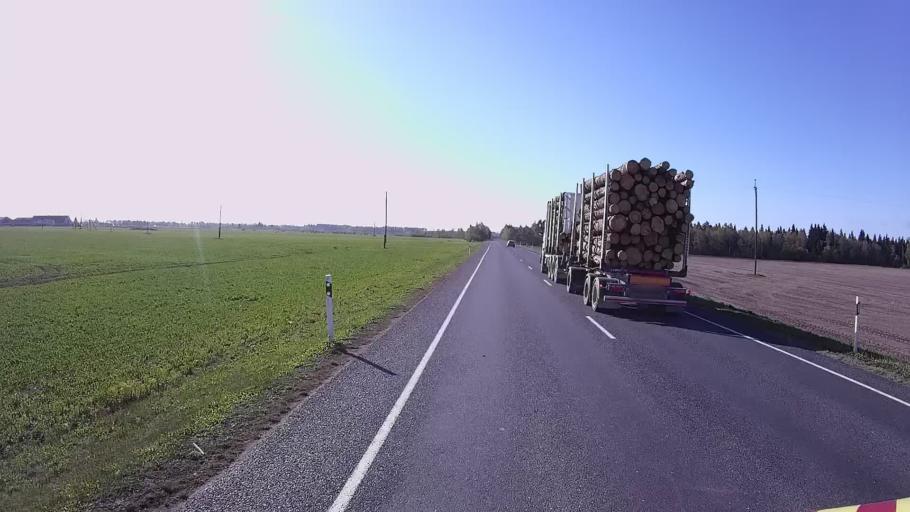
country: EE
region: Viljandimaa
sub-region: Vohma linn
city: Vohma
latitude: 58.7473
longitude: 25.5719
